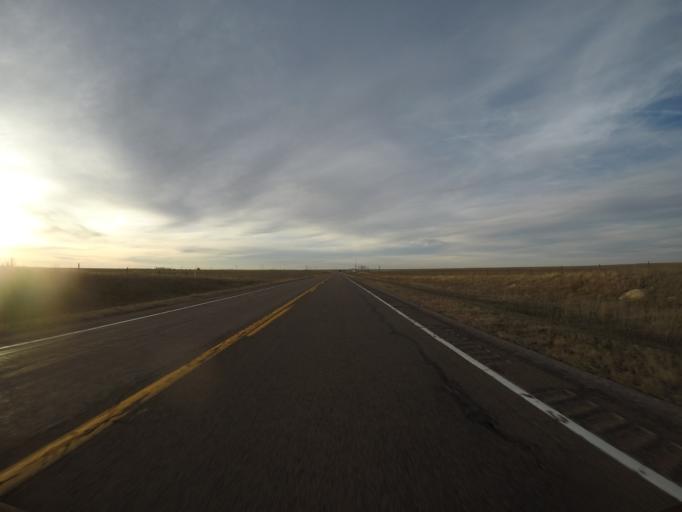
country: US
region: Colorado
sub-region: Washington County
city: Akron
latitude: 39.7369
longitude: -103.1732
